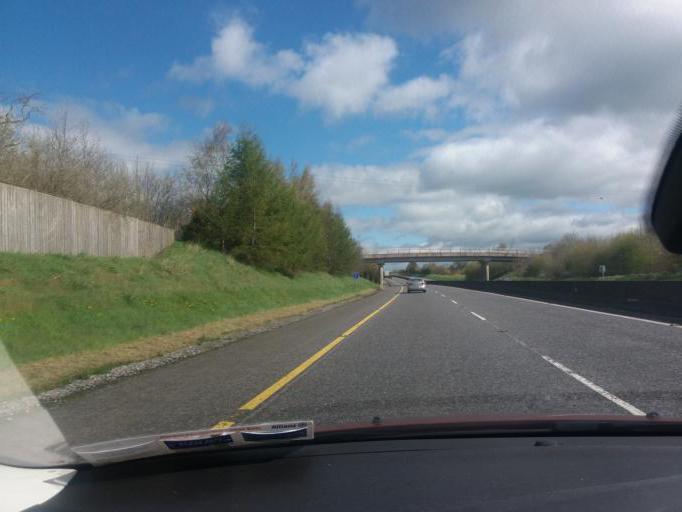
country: IE
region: Munster
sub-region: County Cork
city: Rathcormac
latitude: 52.0801
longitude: -8.2982
